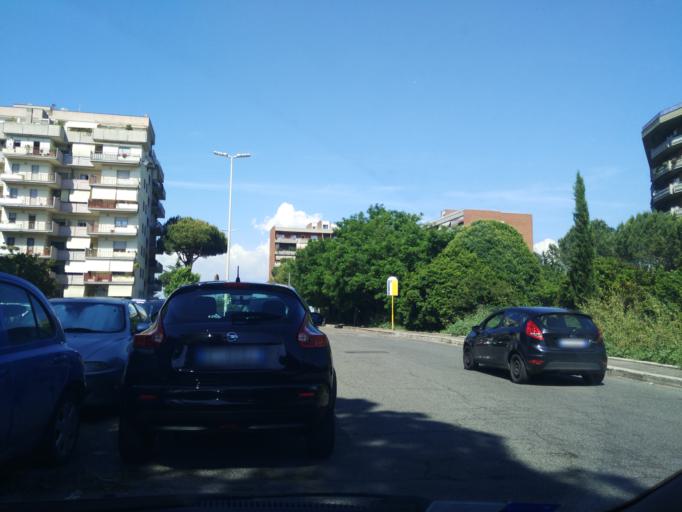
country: IT
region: Latium
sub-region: Citta metropolitana di Roma Capitale
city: Vitinia
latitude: 41.8098
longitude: 12.4362
